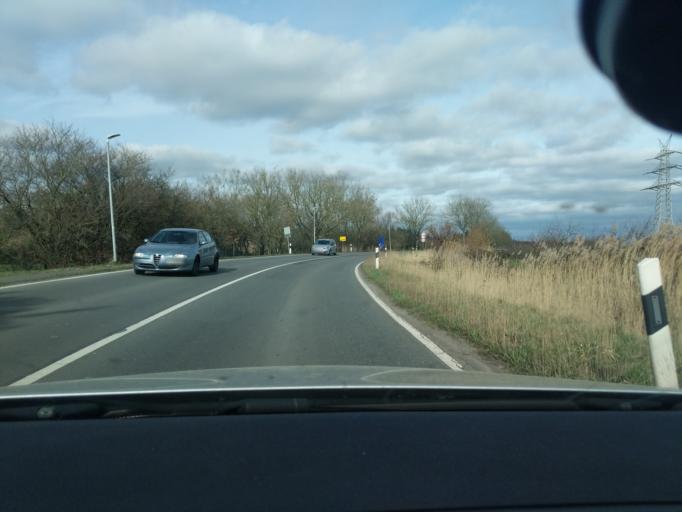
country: DE
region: Lower Saxony
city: Stade
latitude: 53.6571
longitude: 9.4760
